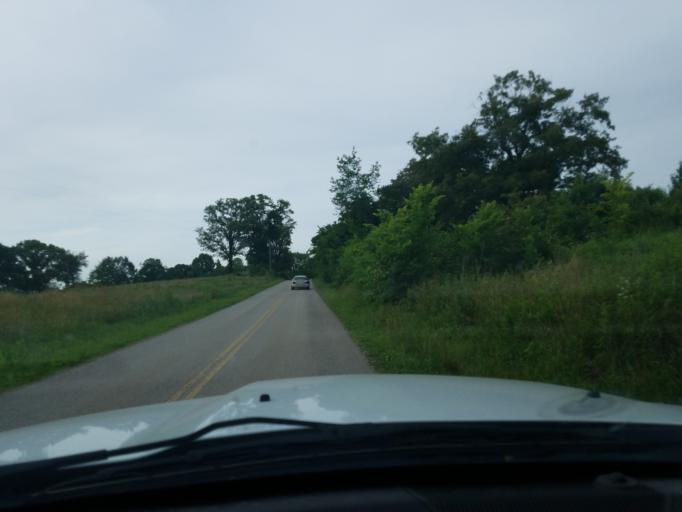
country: US
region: Tennessee
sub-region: Putnam County
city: Baxter
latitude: 36.1262
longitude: -85.5813
